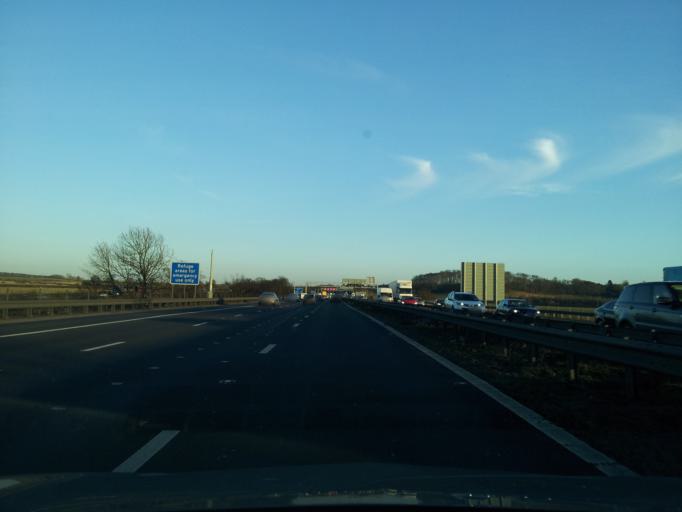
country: GB
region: England
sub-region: Central Bedfordshire
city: Ridgmont
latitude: 52.0235
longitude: -0.5908
